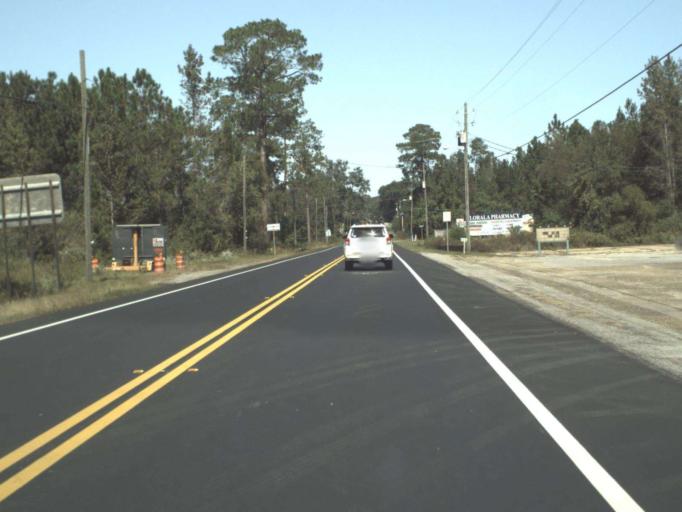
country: US
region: Alabama
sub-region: Covington County
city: Florala
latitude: 30.9893
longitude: -86.3092
